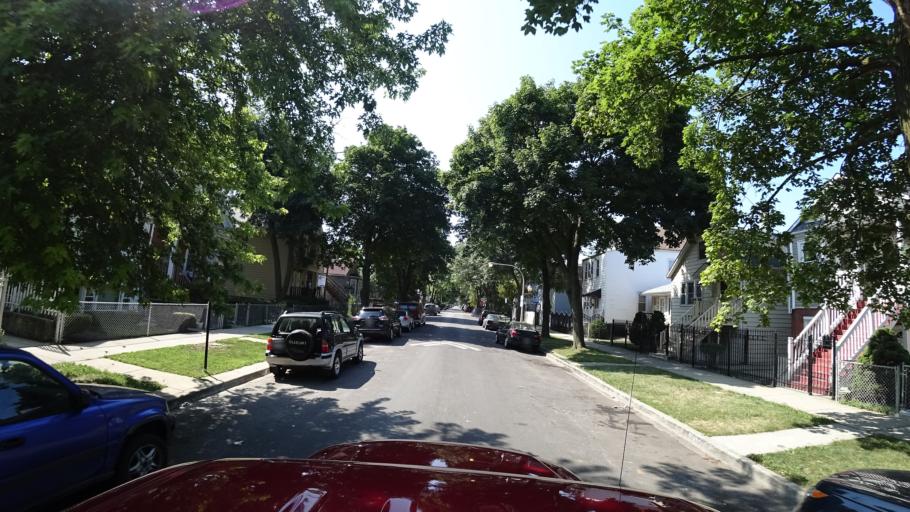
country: US
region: Illinois
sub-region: Cook County
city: Chicago
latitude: 41.8165
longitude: -87.6860
